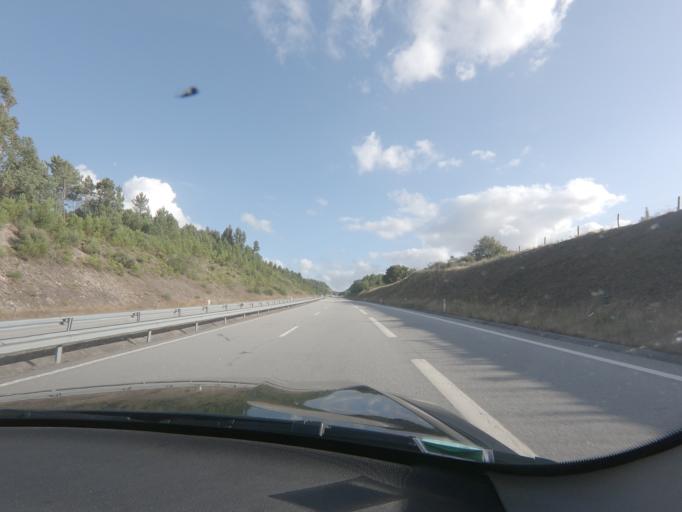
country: PT
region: Viseu
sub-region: Viseu
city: Campo
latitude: 40.7915
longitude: -7.9288
